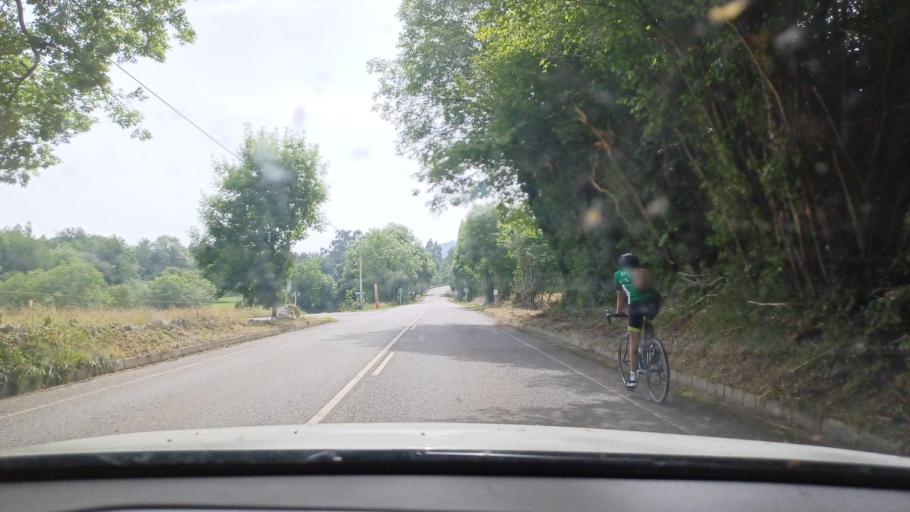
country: ES
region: Asturias
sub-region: Province of Asturias
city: Ribadesella
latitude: 43.4438
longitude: -5.0016
